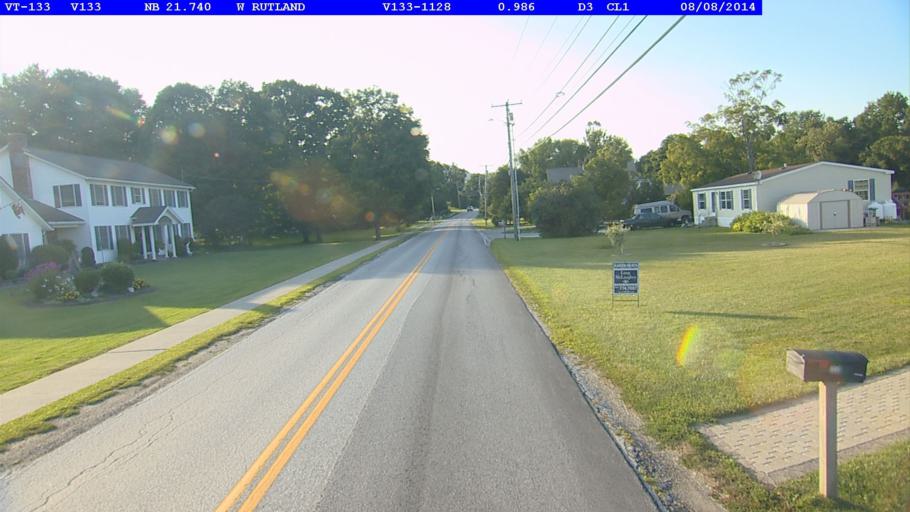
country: US
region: Vermont
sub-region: Rutland County
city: West Rutland
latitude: 43.5830
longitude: -73.0425
